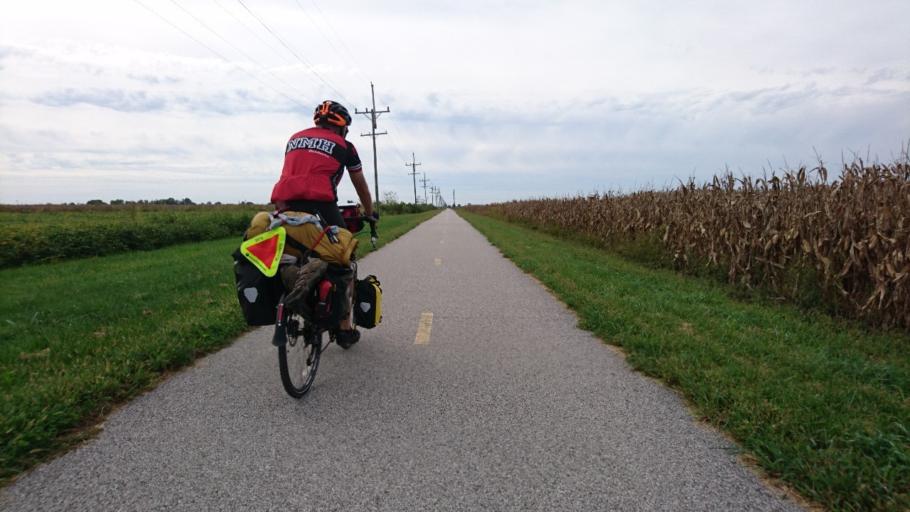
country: US
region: Illinois
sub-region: Madison County
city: Worden
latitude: 38.9080
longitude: -89.8379
